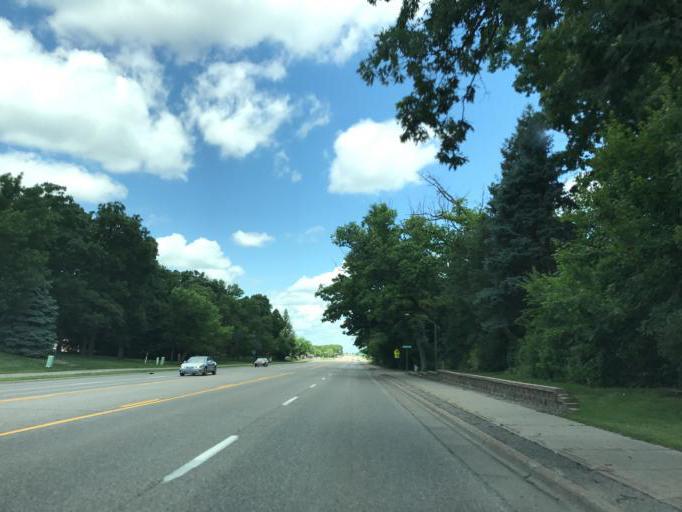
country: US
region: Minnesota
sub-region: Hennepin County
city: Maple Grove
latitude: 45.0747
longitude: -93.4311
